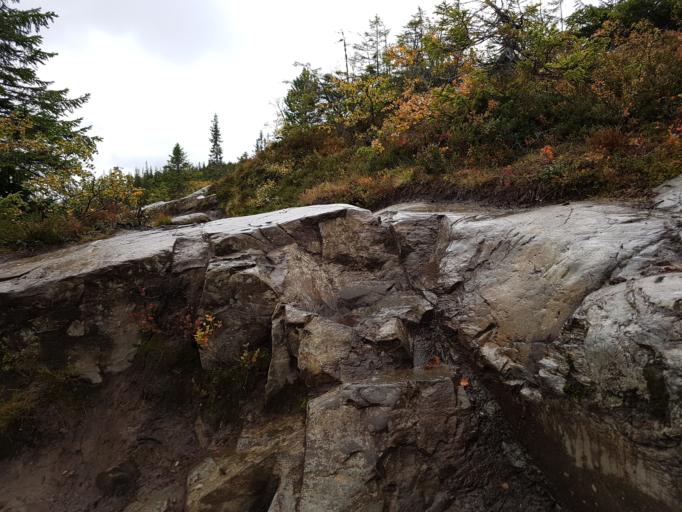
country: NO
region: Sor-Trondelag
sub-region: Melhus
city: Melhus
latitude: 63.4093
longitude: 10.2070
